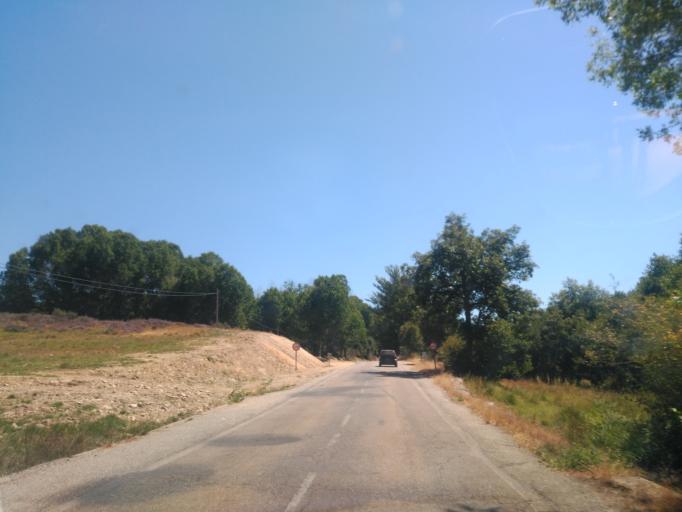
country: ES
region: Castille and Leon
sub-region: Provincia de Zamora
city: Galende
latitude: 42.0876
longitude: -6.6665
